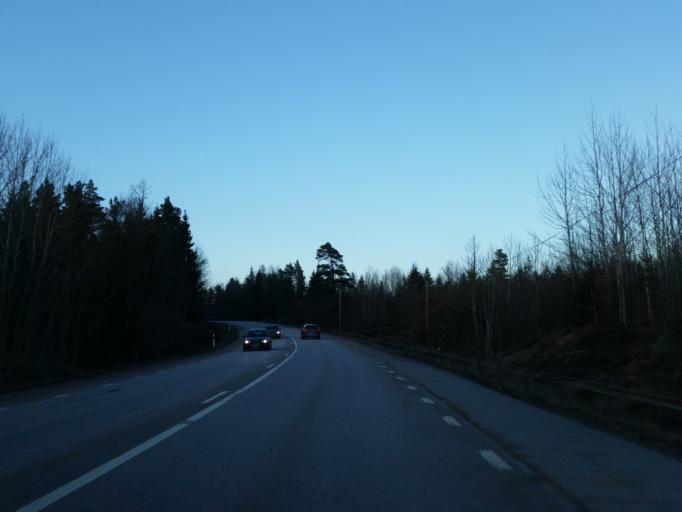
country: SE
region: Kalmar
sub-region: Oskarshamns Kommun
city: Oskarshamn
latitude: 57.4332
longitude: 16.4890
